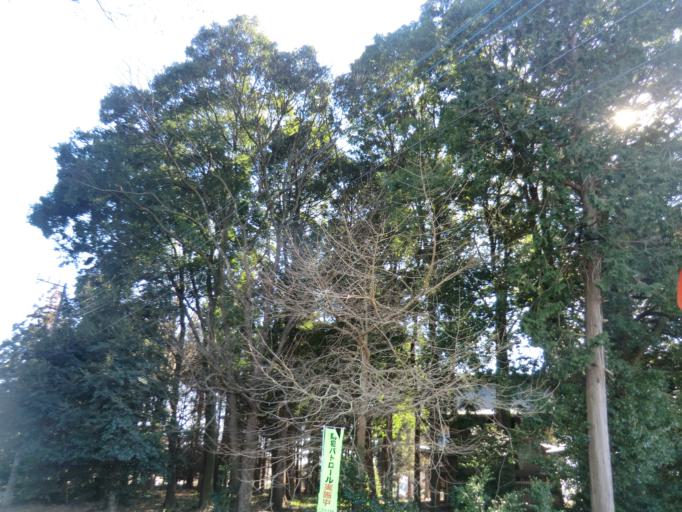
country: JP
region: Ibaraki
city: Naka
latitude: 36.0711
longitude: 140.1116
